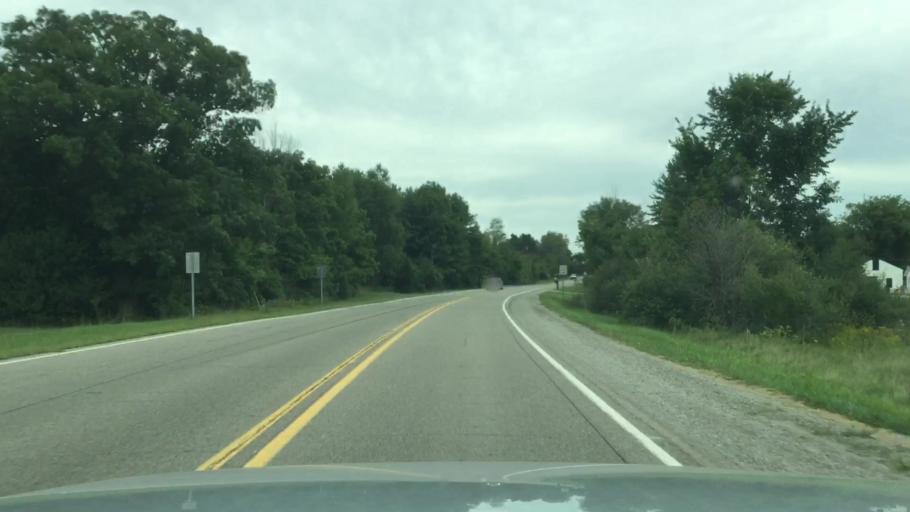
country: US
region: Michigan
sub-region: Shiawassee County
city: Durand
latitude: 42.9566
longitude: -83.9195
